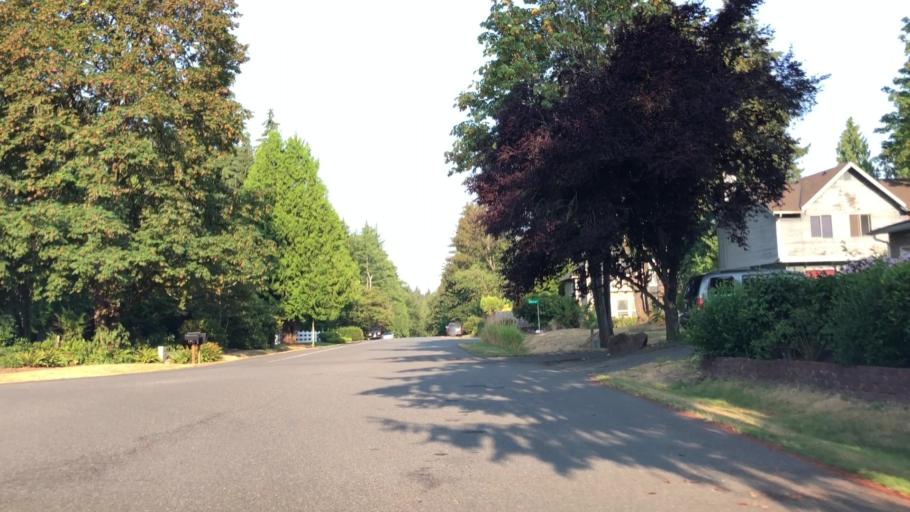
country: US
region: Washington
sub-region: King County
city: Cottage Lake
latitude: 47.7217
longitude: -122.1019
